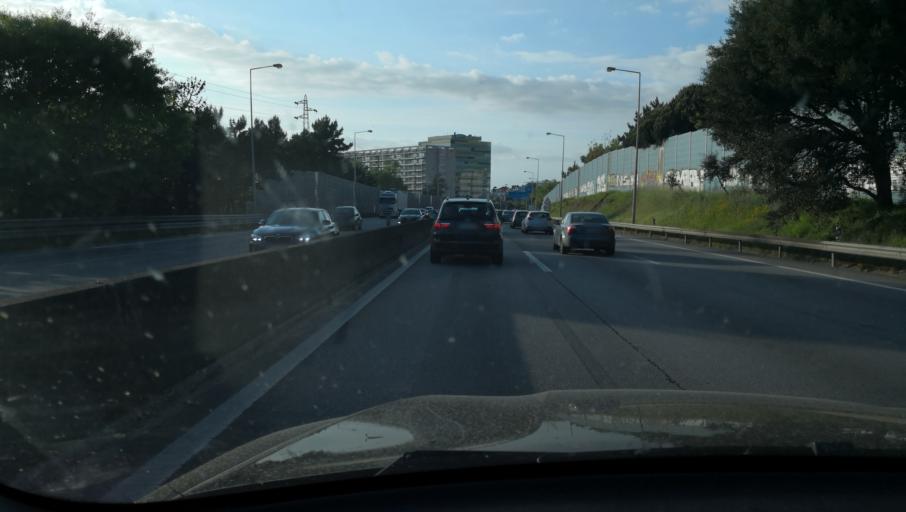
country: PT
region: Porto
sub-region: Vila Nova de Gaia
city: Vila Nova de Gaia
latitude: 41.1390
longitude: -8.6369
